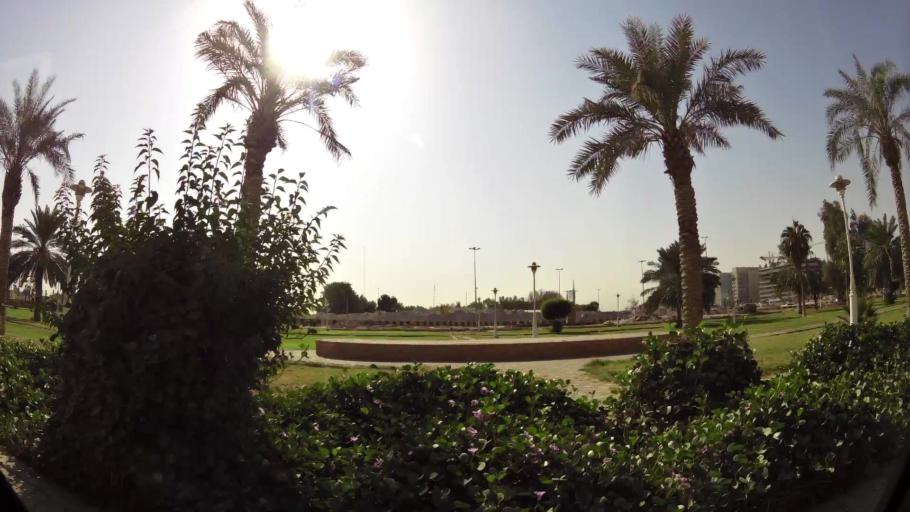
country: KW
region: Al Asimah
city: Ash Shamiyah
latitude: 29.3531
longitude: 47.9454
